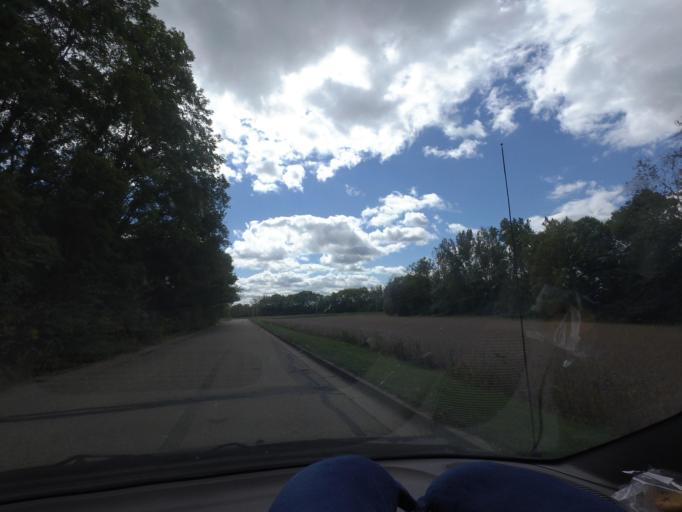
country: US
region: Ohio
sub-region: Clark County
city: Park Layne
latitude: 39.8716
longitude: -84.0587
